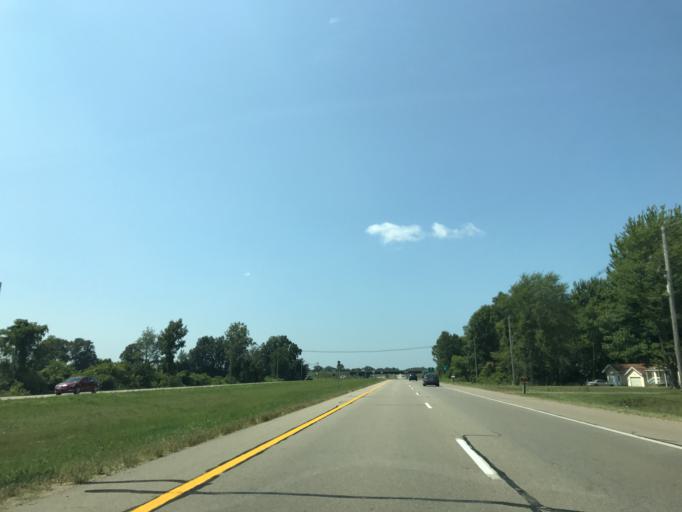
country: US
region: Michigan
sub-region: Berrien County
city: Buchanan
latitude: 41.8052
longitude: -86.3085
